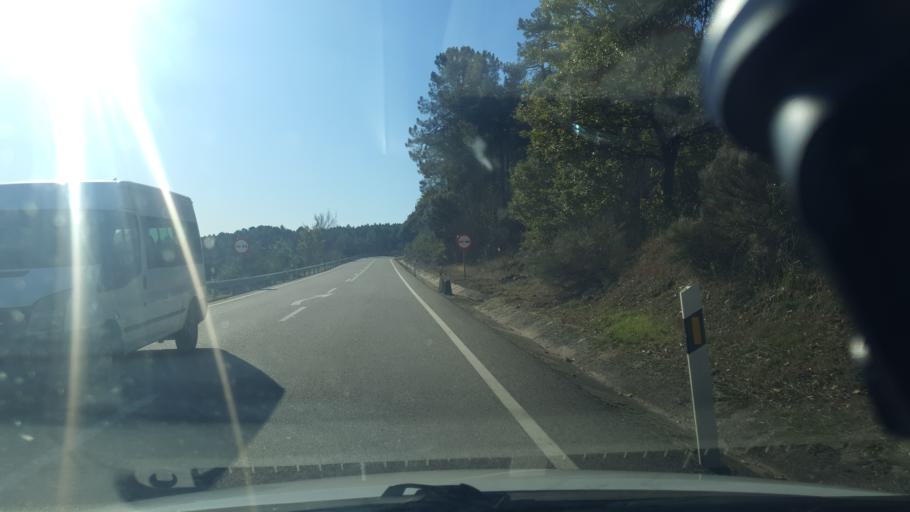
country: ES
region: Castille and Leon
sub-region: Provincia de Avila
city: Arenas de San Pedro
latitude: 40.2047
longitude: -5.0430
